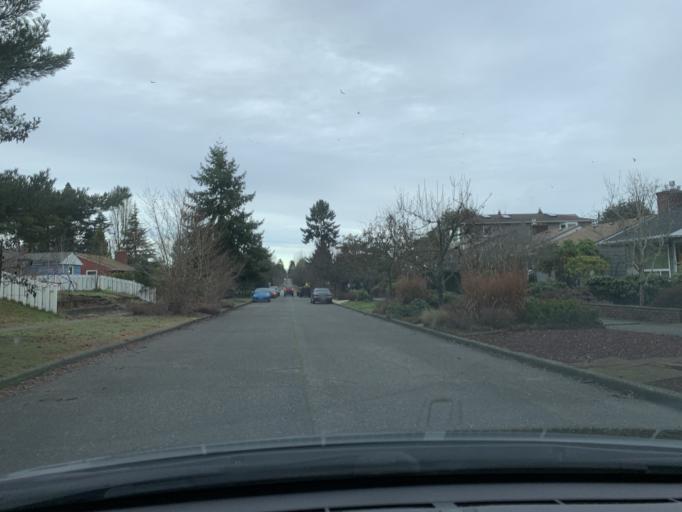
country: US
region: Washington
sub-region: King County
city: White Center
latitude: 47.5691
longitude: -122.3948
